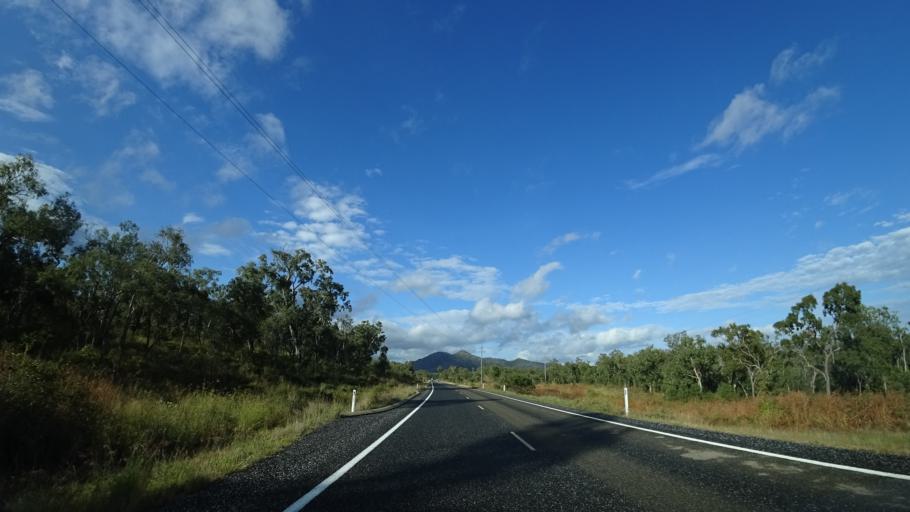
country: AU
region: Queensland
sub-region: Cook
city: Cooktown
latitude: -15.6078
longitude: 145.2218
